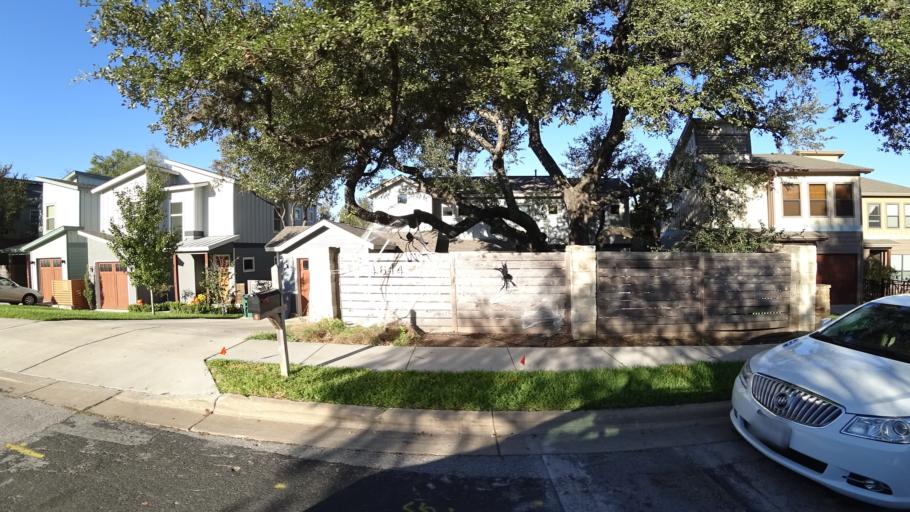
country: US
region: Texas
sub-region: Travis County
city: Austin
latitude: 30.2928
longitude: -97.6863
